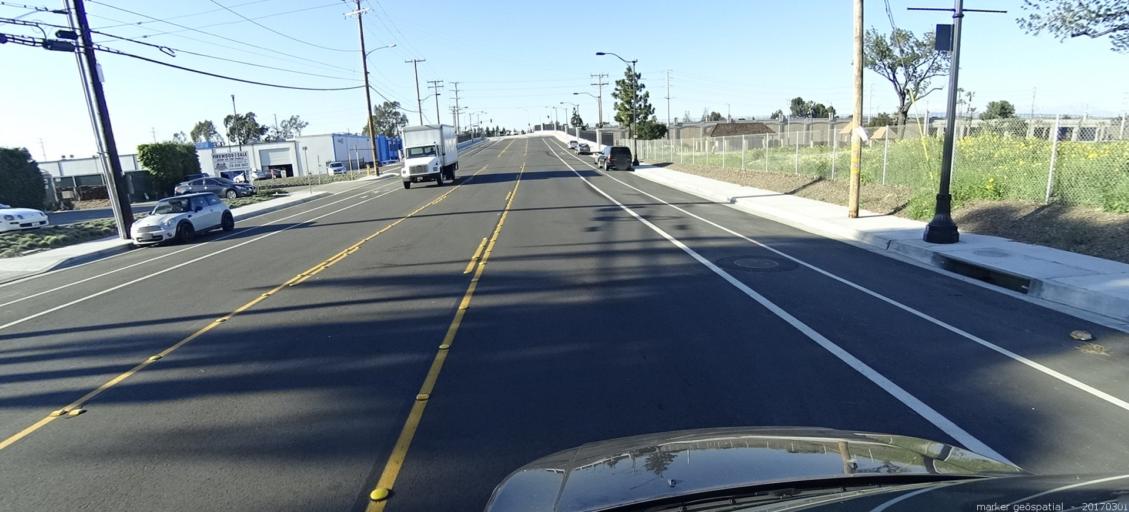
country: US
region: California
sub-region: Orange County
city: Placentia
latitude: 33.8654
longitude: -117.8511
